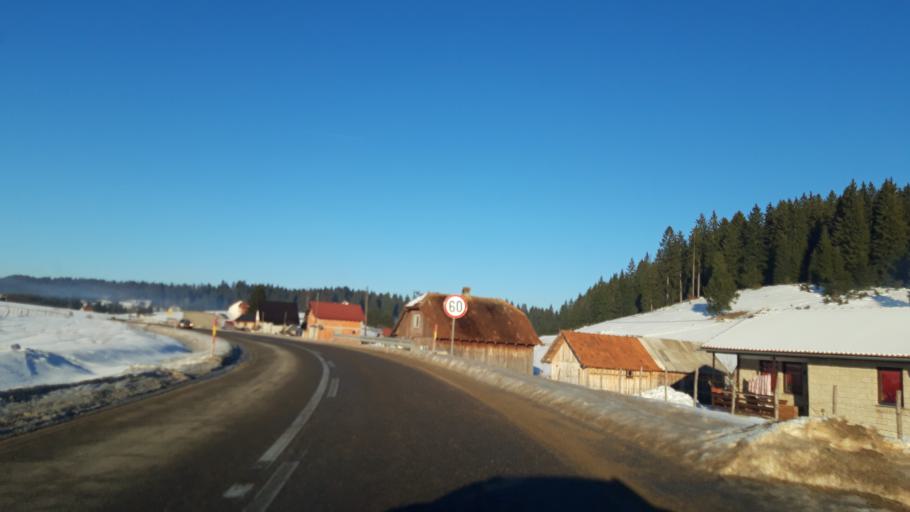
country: BA
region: Republika Srpska
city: Han Pijesak
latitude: 44.1023
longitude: 18.9693
